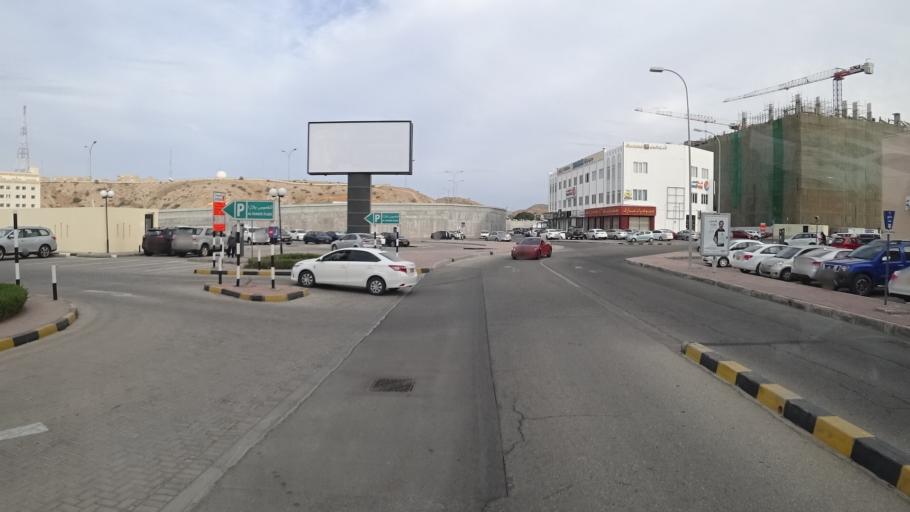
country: OM
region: Muhafazat Masqat
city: Muscat
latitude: 23.6117
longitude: 58.4965
